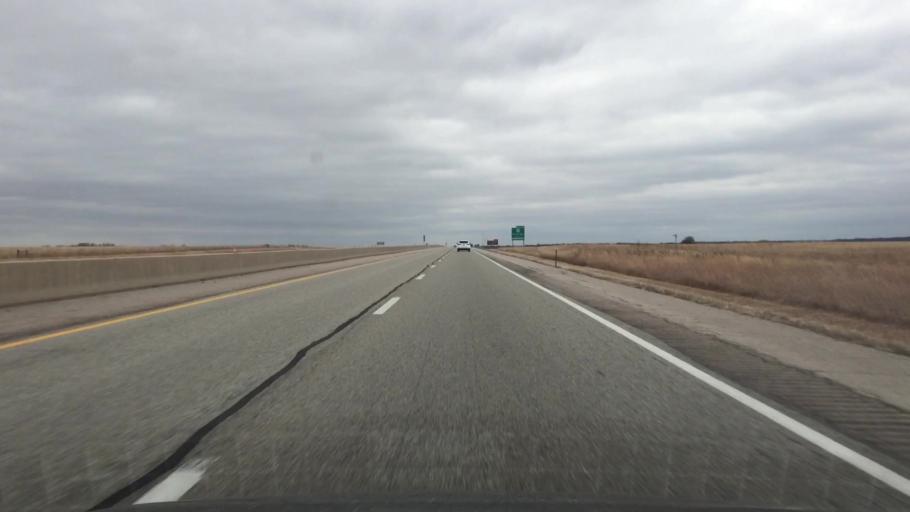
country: US
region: Kansas
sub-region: Butler County
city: El Dorado
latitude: 37.8896
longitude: -96.8382
